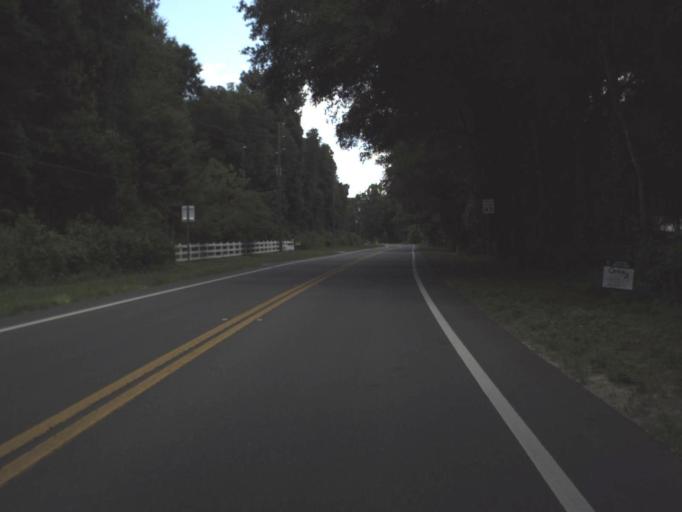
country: US
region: Florida
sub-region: Clay County
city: Keystone Heights
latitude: 29.7017
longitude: -82.0422
